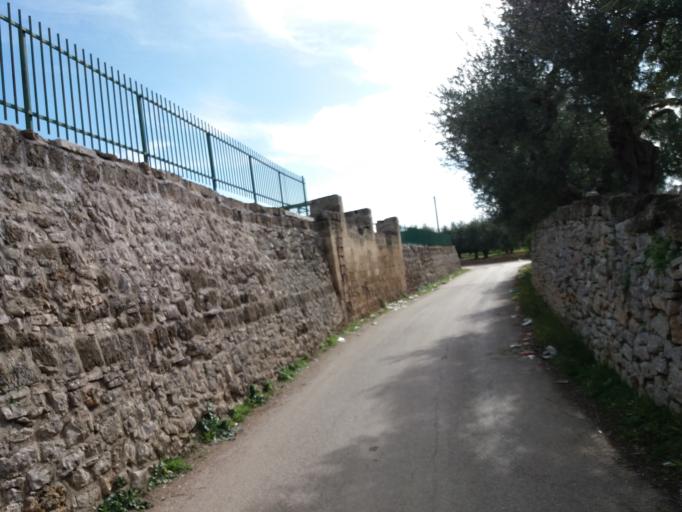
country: IT
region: Apulia
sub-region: Provincia di Barletta - Andria - Trani
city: Andria
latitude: 41.2146
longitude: 16.3082
